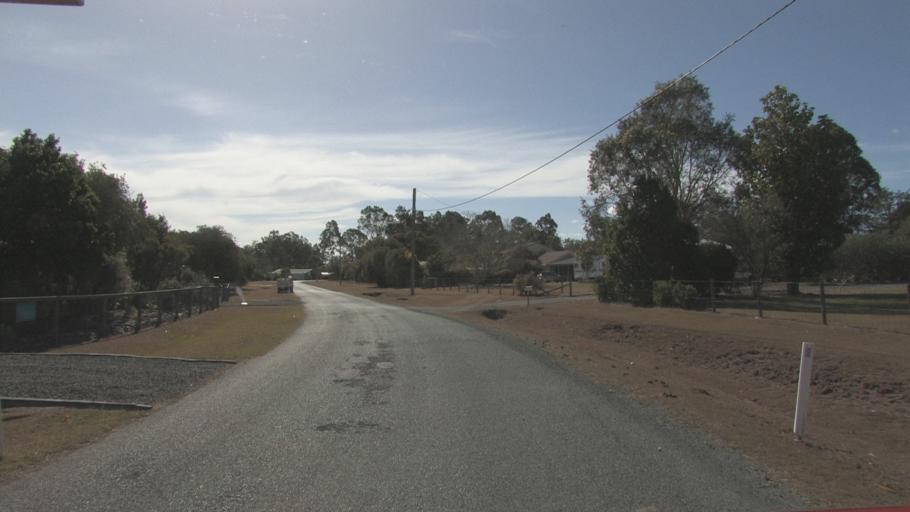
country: AU
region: Queensland
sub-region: Logan
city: Cedar Vale
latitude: -27.8703
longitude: 152.9727
